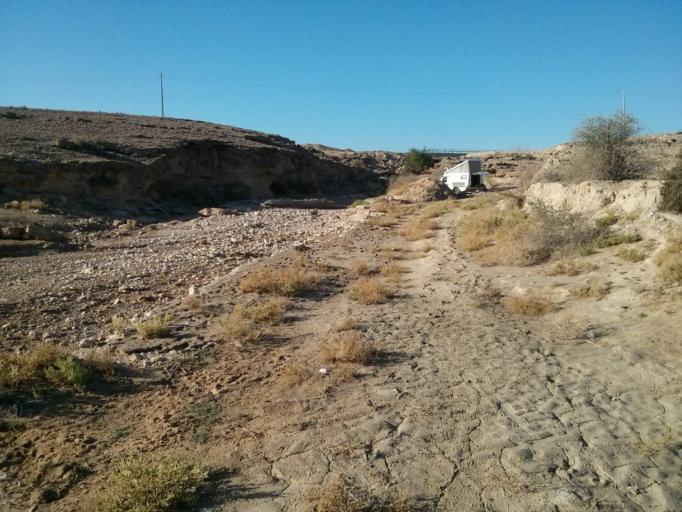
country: IR
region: Hormozgan
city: Bastak
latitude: 27.3895
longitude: 54.3088
